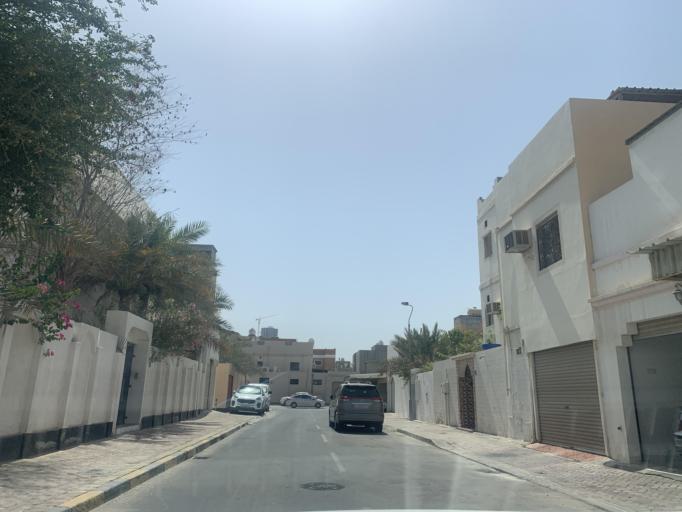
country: BH
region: Manama
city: Jidd Hafs
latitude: 26.2259
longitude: 50.5484
